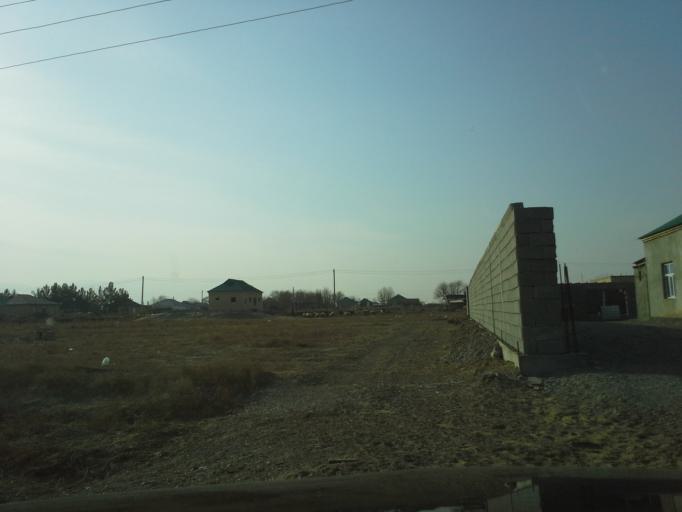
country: TM
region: Ahal
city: Abadan
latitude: 38.1816
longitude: 58.0484
